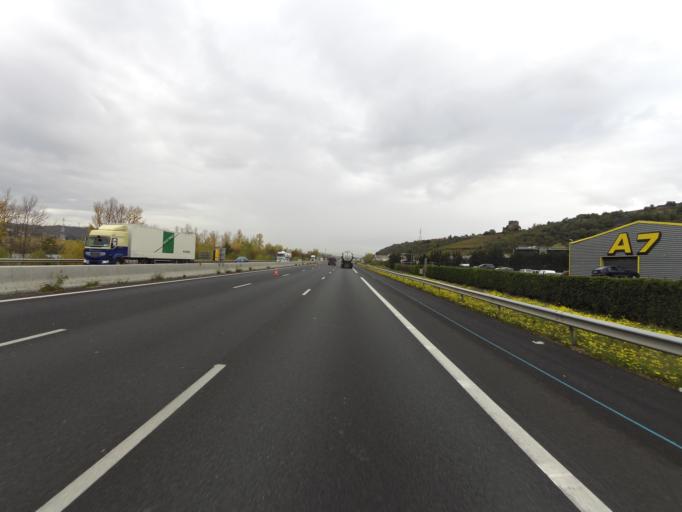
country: FR
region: Rhone-Alpes
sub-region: Departement du Rhone
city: Loire-sur-Rhone
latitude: 45.5550
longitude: 4.8264
